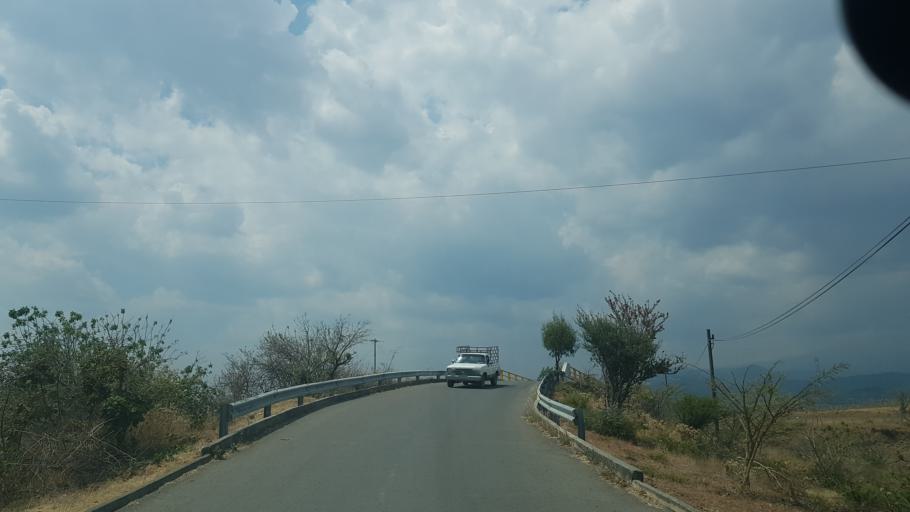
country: MX
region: Puebla
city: San Juan Amecac
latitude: 18.8167
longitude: -98.6520
